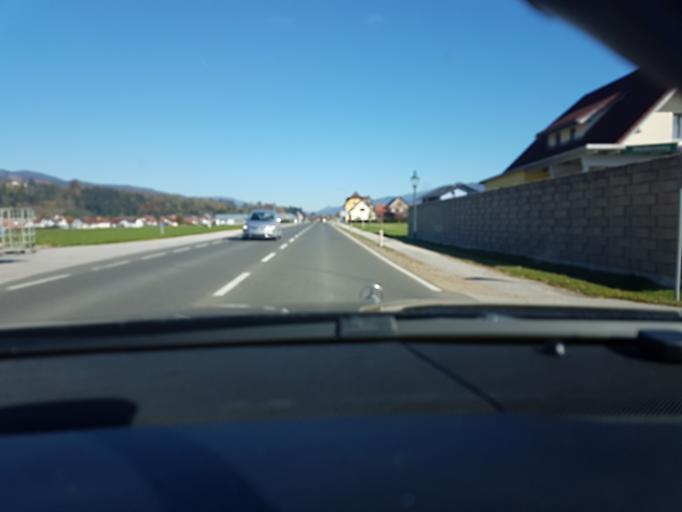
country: AT
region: Styria
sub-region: Politischer Bezirk Bruck-Muerzzuschlag
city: Krieglach
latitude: 47.5425
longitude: 15.5390
